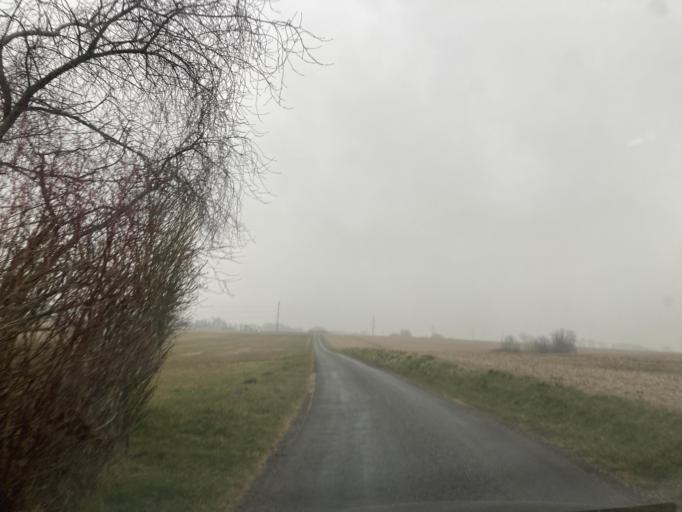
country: DK
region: Zealand
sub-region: Vordingborg Kommune
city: Neder Vindinge
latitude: 55.1596
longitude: 11.8967
